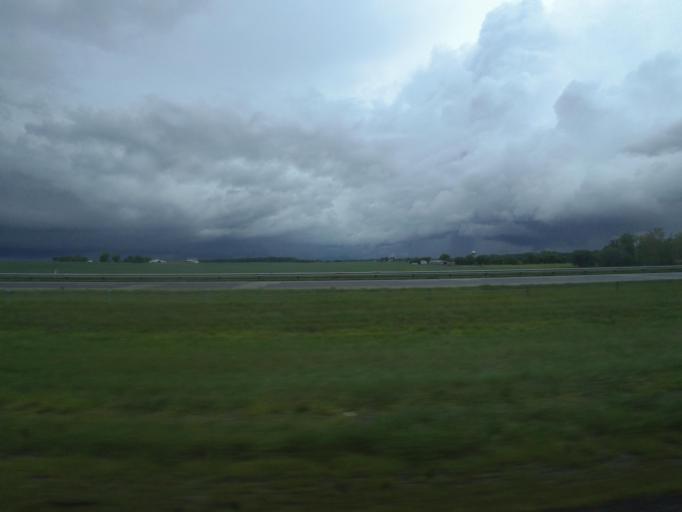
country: US
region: Indiana
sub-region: Wayne County
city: Centerville
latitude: 39.8542
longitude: -85.0782
